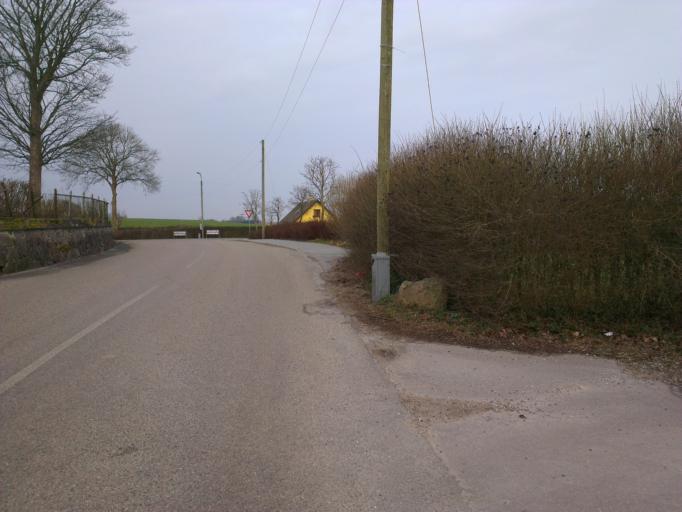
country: DK
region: Capital Region
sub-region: Frederikssund Kommune
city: Skibby
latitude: 55.7624
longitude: 11.8883
